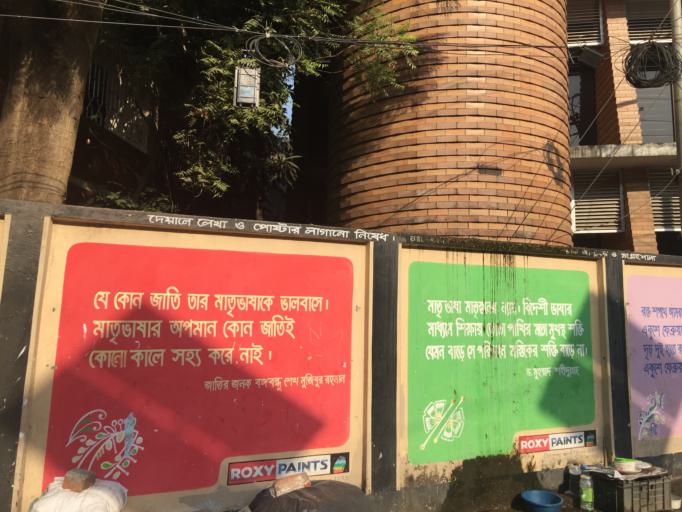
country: BD
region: Dhaka
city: Azimpur
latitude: 23.7277
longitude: 90.3893
